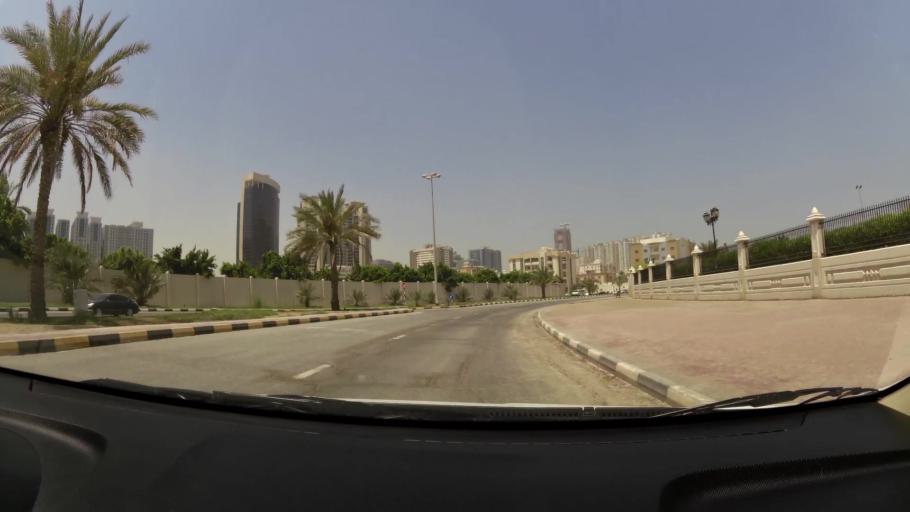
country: AE
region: Ajman
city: Ajman
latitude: 25.3958
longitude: 55.4424
